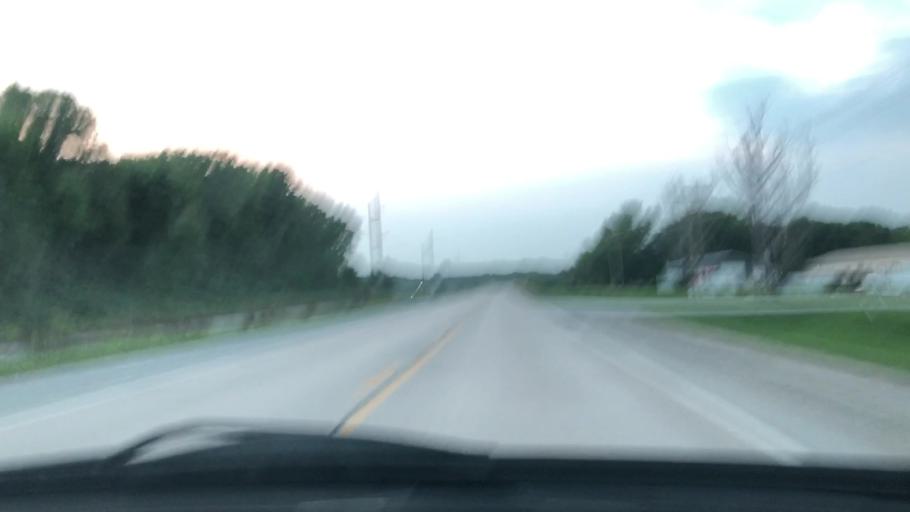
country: US
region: Iowa
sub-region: Johnson County
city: North Liberty
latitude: 41.8038
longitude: -91.6492
